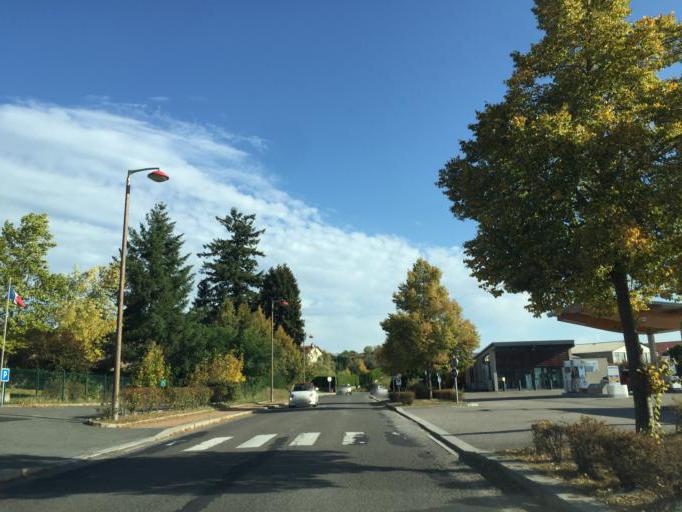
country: FR
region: Rhone-Alpes
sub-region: Departement de la Loire
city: Saint-Bonnet-le-Chateau
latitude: 45.4265
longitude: 4.0637
